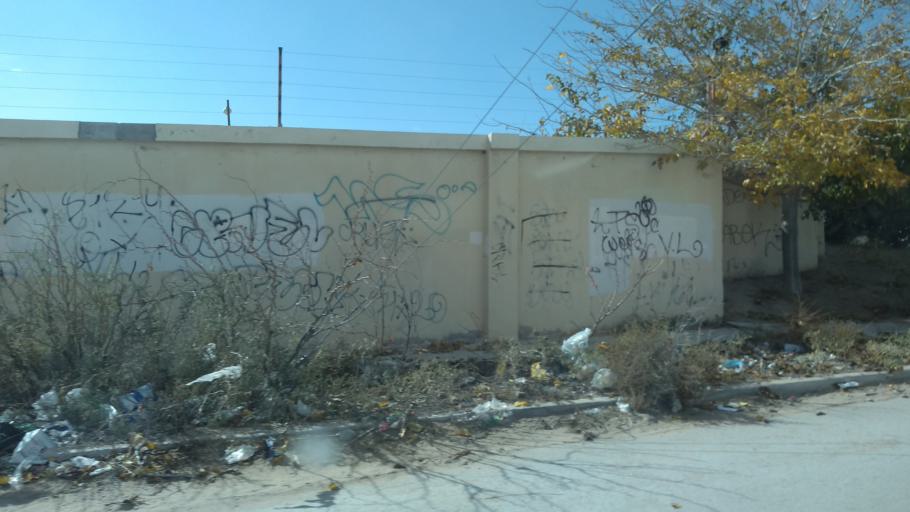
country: US
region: Texas
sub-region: El Paso County
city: San Elizario
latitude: 31.5778
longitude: -106.3288
